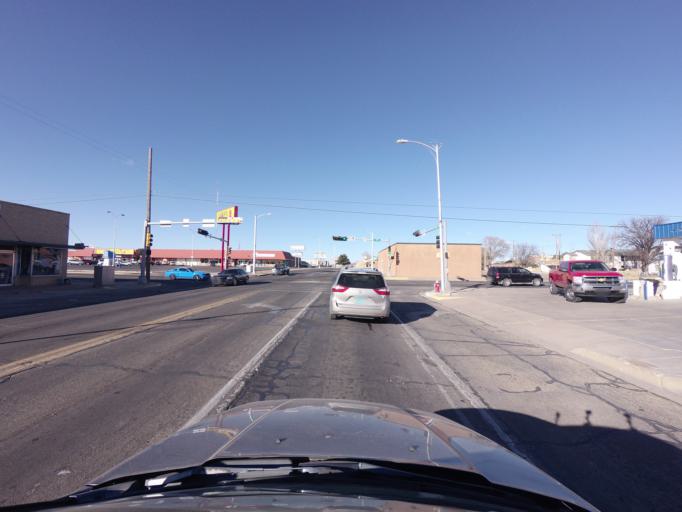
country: US
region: New Mexico
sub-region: Curry County
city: Clovis
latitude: 34.4117
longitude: -103.2053
